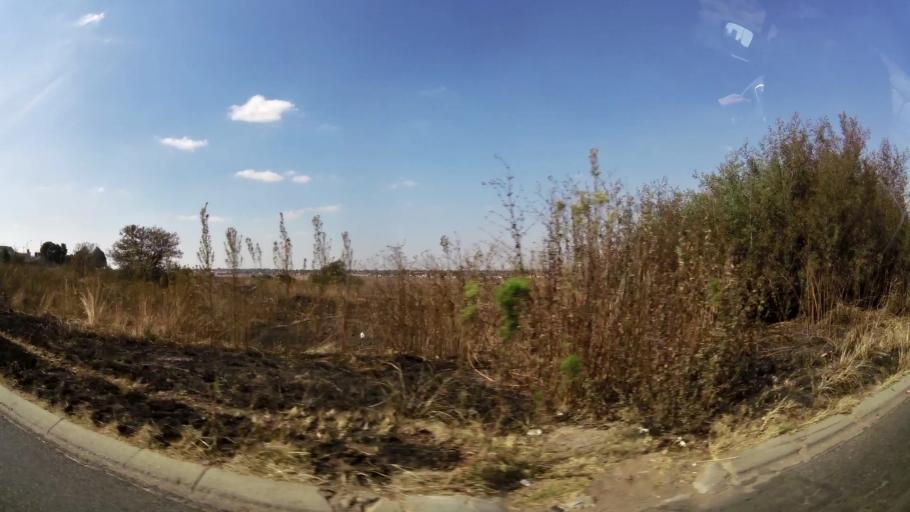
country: ZA
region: Gauteng
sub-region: City of Johannesburg Metropolitan Municipality
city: Roodepoort
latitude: -26.1580
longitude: 27.8046
